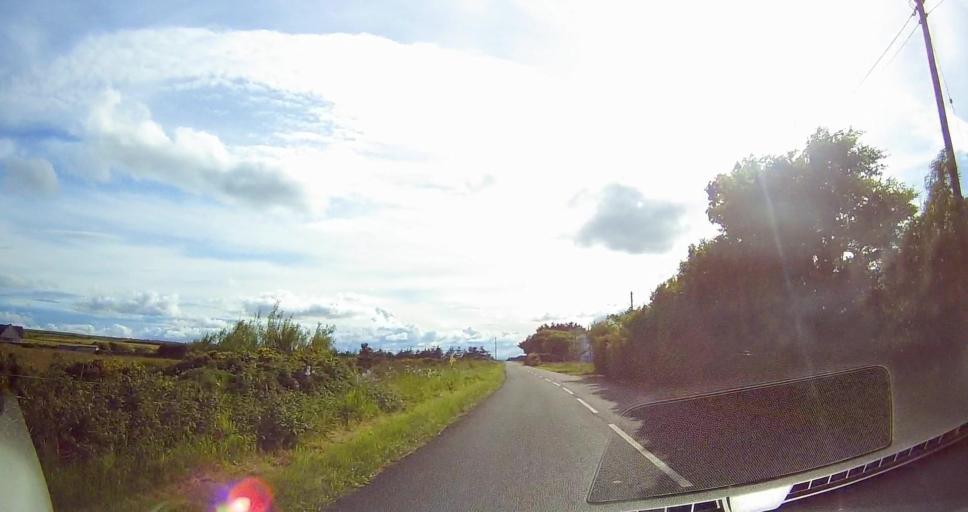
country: GB
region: Scotland
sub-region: Highland
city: Thurso
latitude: 58.6289
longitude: -3.3175
